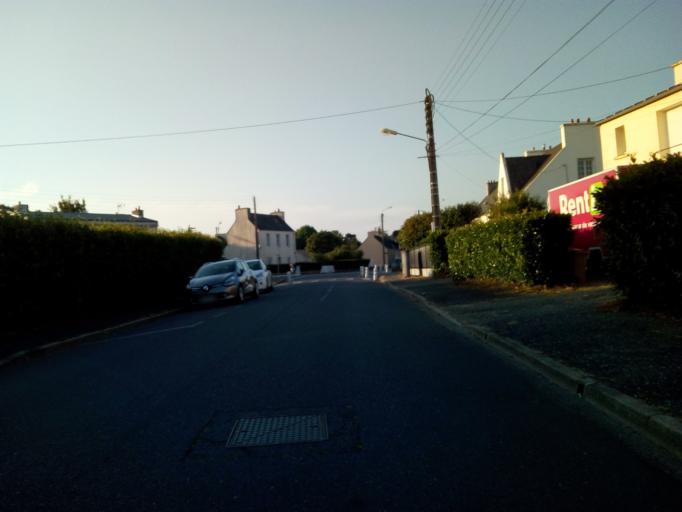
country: FR
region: Brittany
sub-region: Departement du Finistere
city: Landivisiau
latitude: 48.5014
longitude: -4.0785
